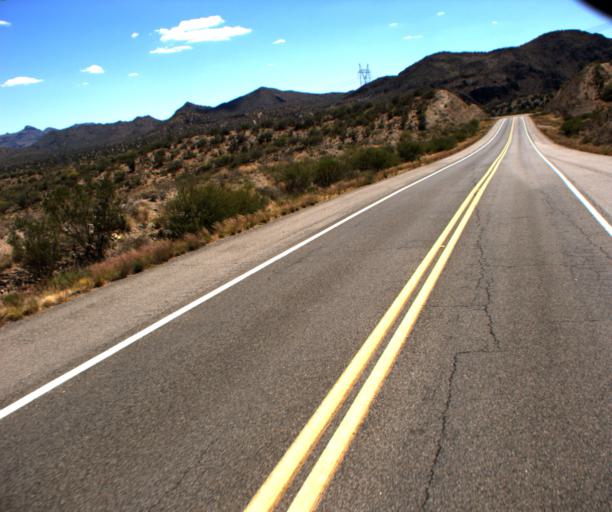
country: US
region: Arizona
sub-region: Yavapai County
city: Bagdad
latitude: 34.4323
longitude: -113.2430
